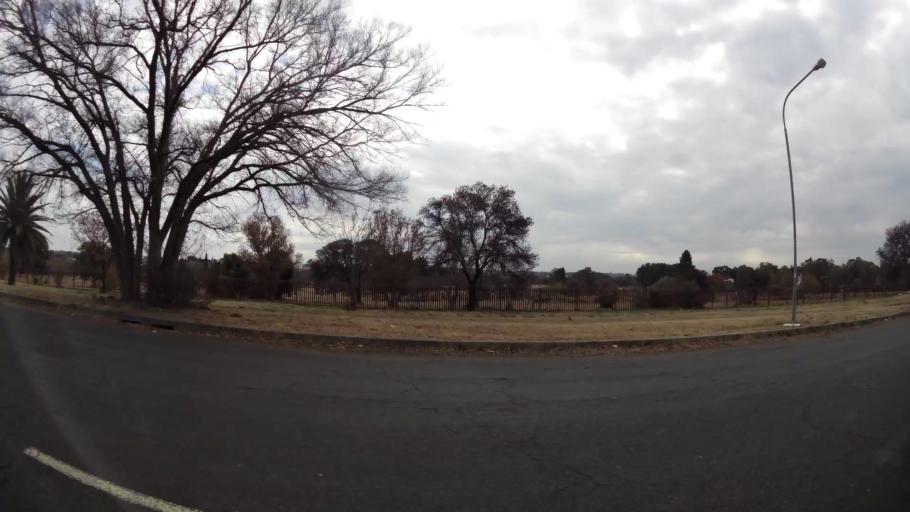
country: ZA
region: Orange Free State
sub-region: Fezile Dabi District Municipality
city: Kroonstad
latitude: -27.6733
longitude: 27.2410
